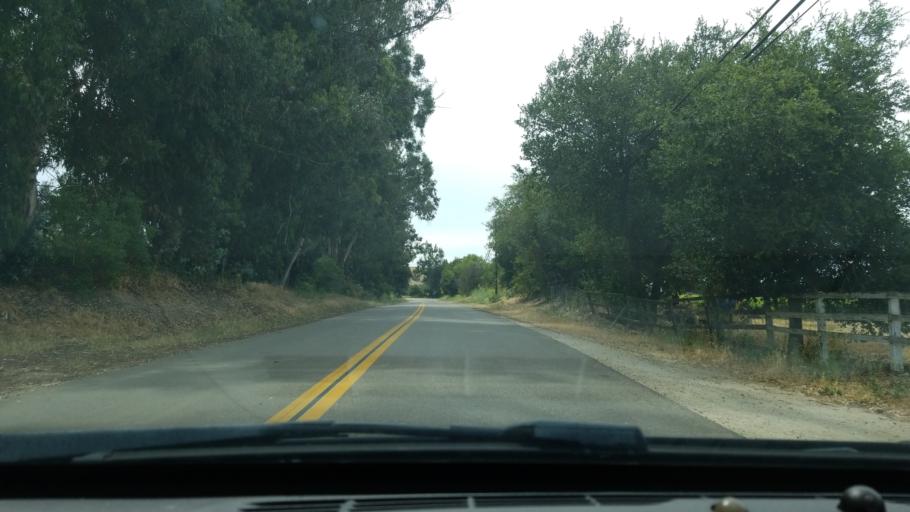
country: US
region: California
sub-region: Santa Barbara County
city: Los Alamos
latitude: 34.8581
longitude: -120.2737
